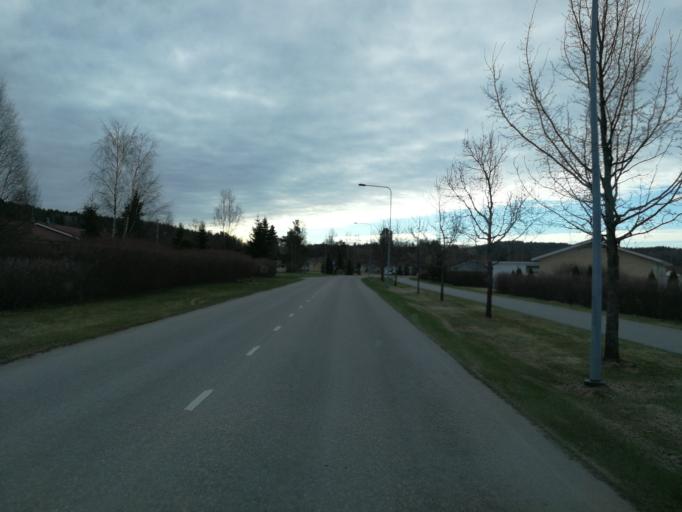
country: FI
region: Varsinais-Suomi
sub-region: Salo
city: Salo
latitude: 60.3788
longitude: 23.1569
